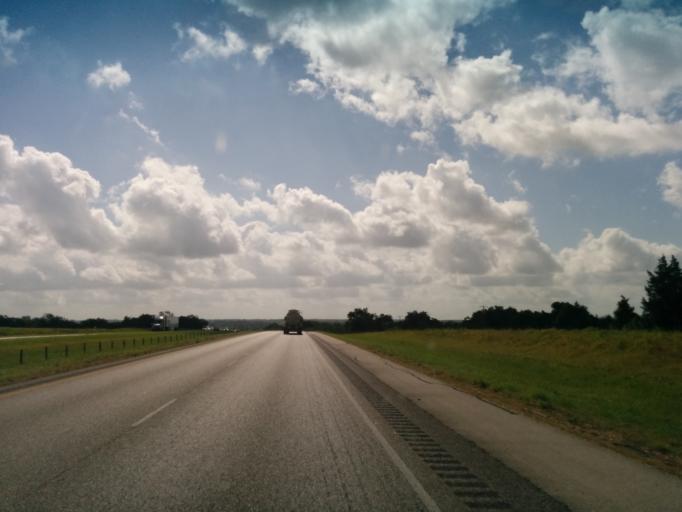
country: US
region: Texas
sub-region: Fayette County
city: Schulenburg
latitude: 29.6891
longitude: -96.9621
